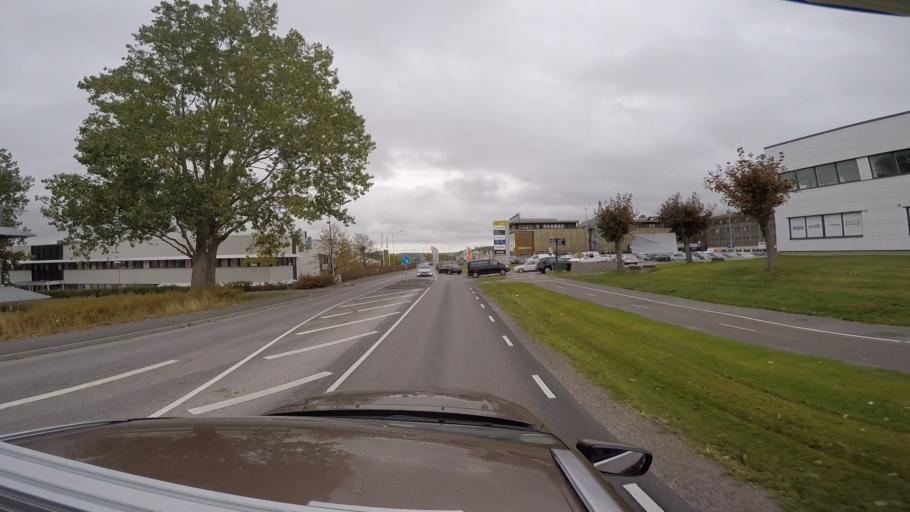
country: SE
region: Vaestra Goetaland
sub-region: Goteborg
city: Majorna
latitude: 57.6414
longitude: 11.9451
